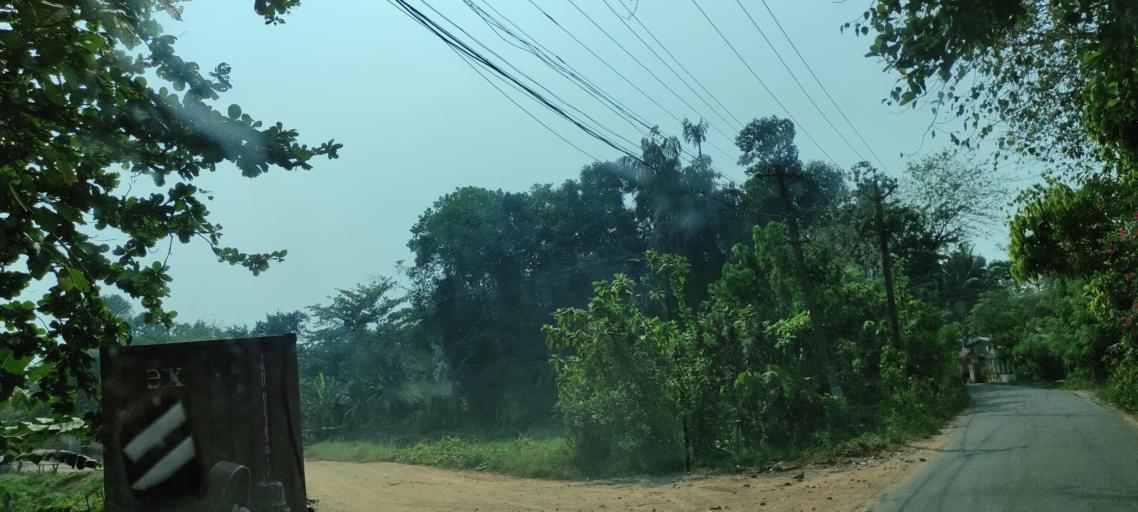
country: IN
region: Kerala
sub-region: Pattanamtitta
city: Tiruvalla
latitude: 9.3456
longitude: 76.5448
